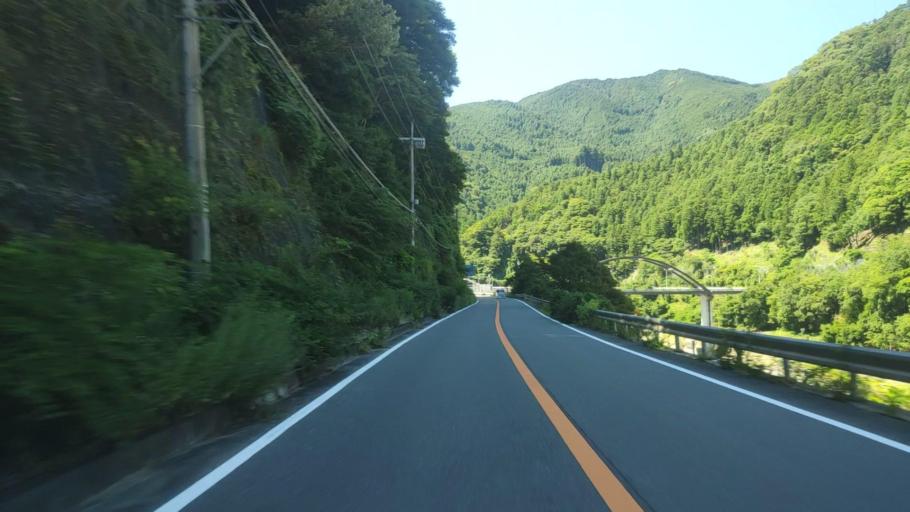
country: JP
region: Nara
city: Yoshino-cho
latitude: 34.3127
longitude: 135.9908
